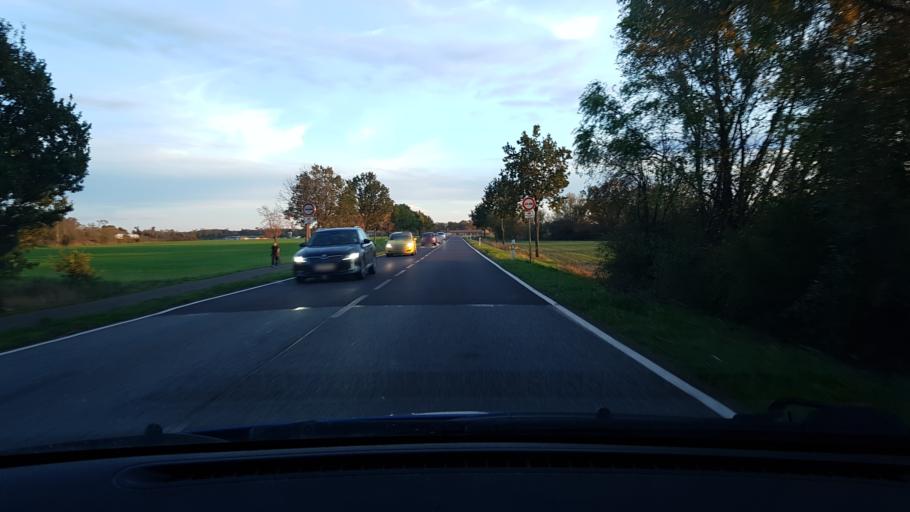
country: DE
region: Saxony-Anhalt
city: Wahlitz
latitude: 52.1295
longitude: 11.7609
